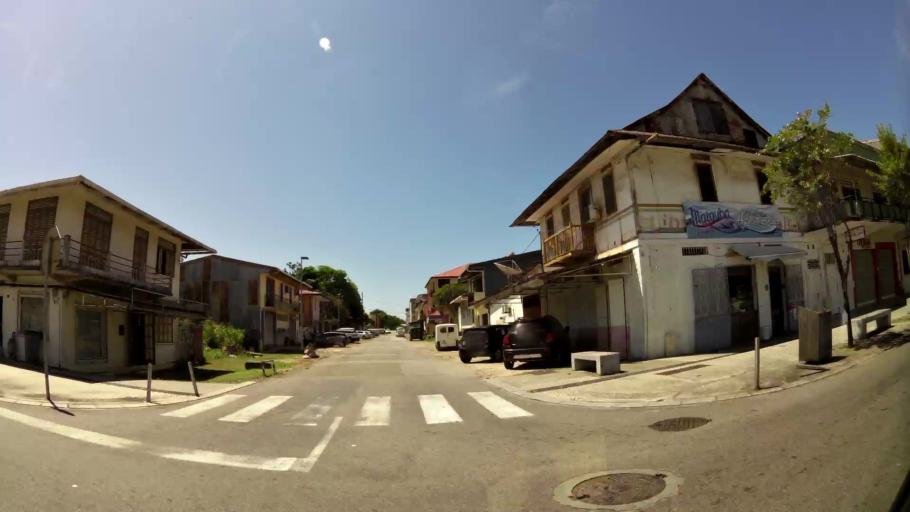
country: GF
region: Guyane
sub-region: Guyane
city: Cayenne
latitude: 4.9405
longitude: -52.3250
